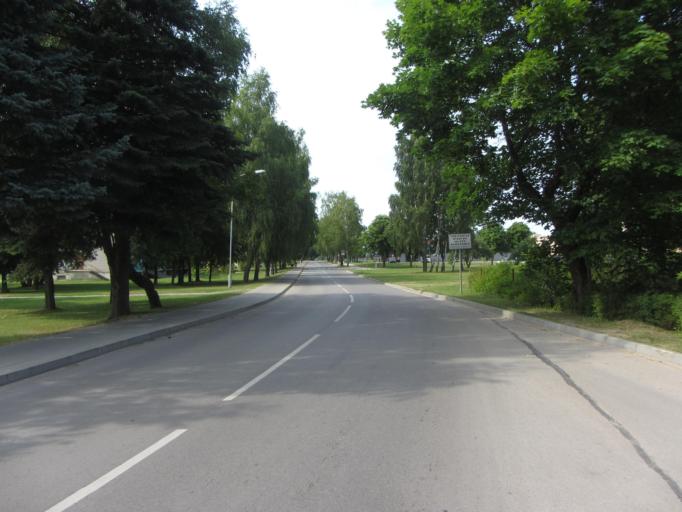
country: LT
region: Alytaus apskritis
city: Druskininkai
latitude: 54.0486
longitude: 24.0588
